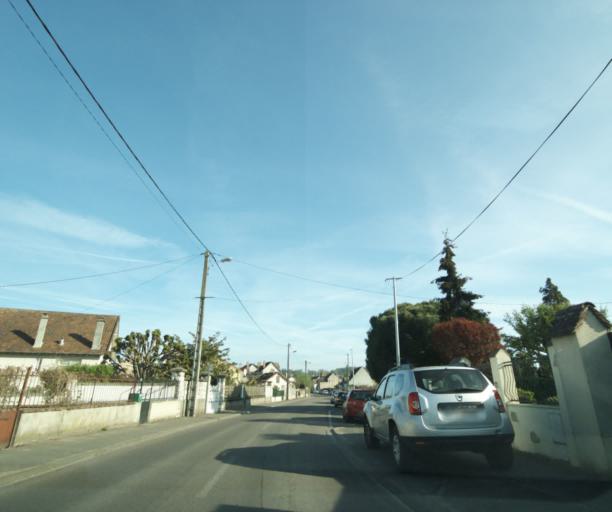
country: FR
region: Ile-de-France
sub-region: Departement de Seine-et-Marne
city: Saint-Mammes
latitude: 48.3834
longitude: 2.8111
